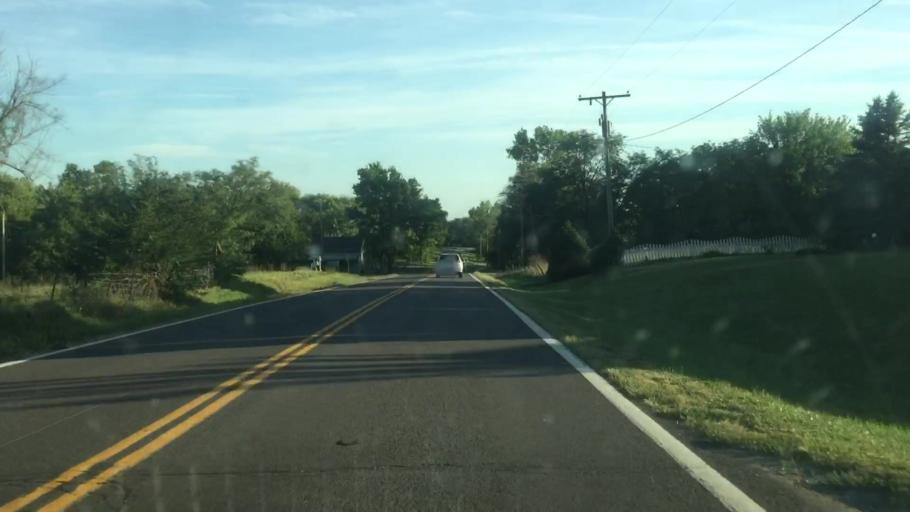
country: US
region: Kansas
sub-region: Brown County
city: Horton
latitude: 39.5545
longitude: -95.5247
